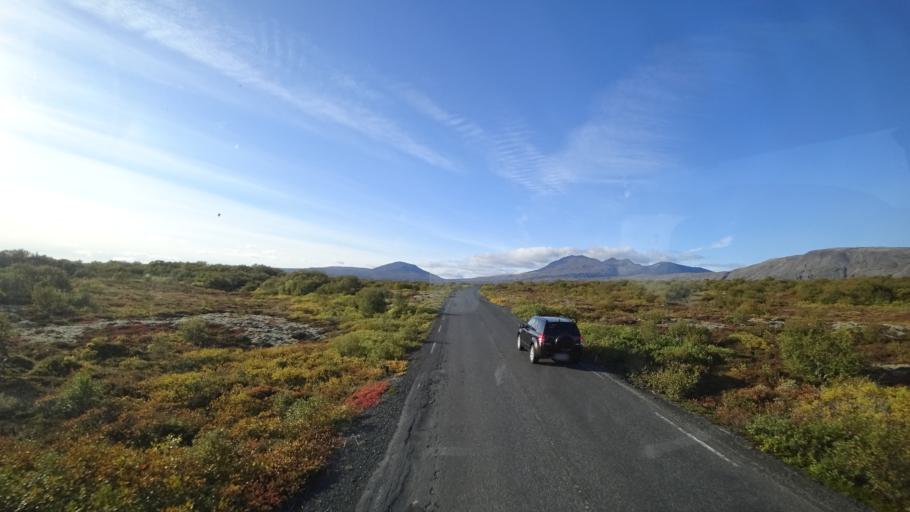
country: IS
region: South
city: Hveragerdi
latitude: 64.2655
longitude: -21.0581
